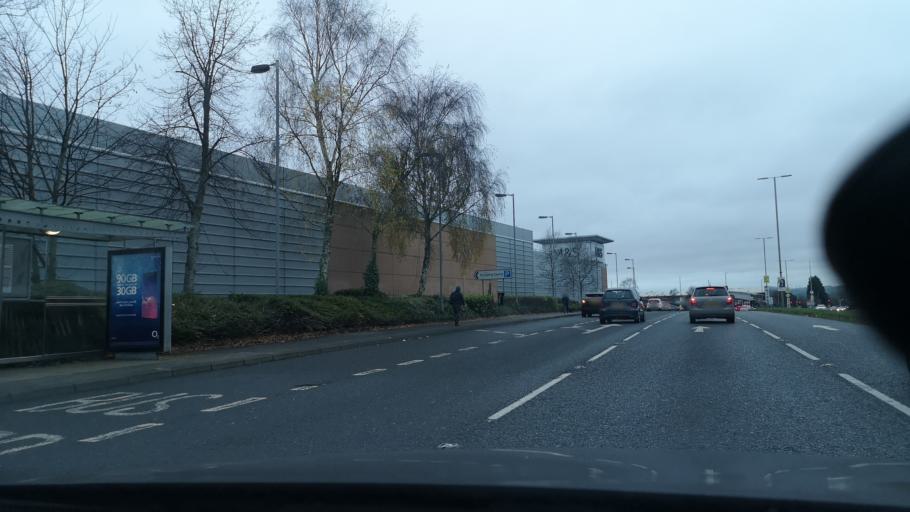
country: GB
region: Northern Ireland
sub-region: Castlereagh District
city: Castlereagh
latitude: 54.5623
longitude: -5.9087
